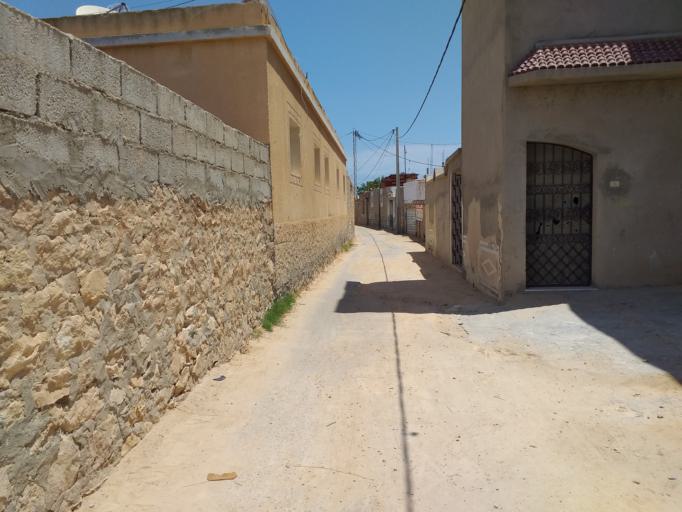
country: TN
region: Qabis
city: Gabes
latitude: 33.9428
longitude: 10.0606
